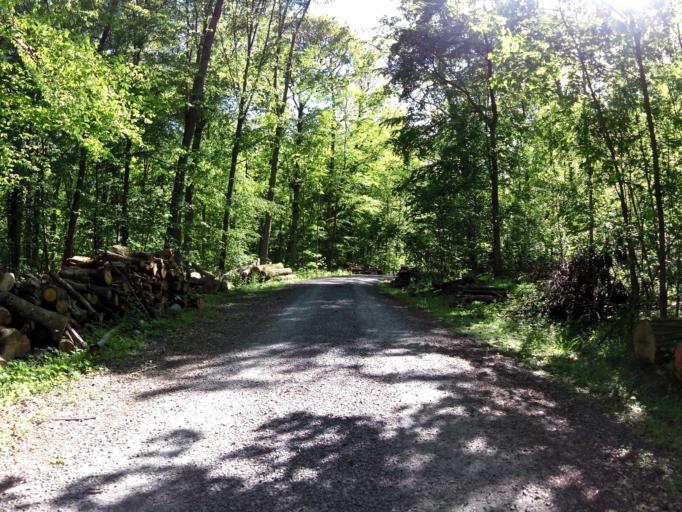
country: DE
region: Bavaria
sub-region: Regierungsbezirk Unterfranken
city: Reichenberg
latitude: 49.7538
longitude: 9.9113
